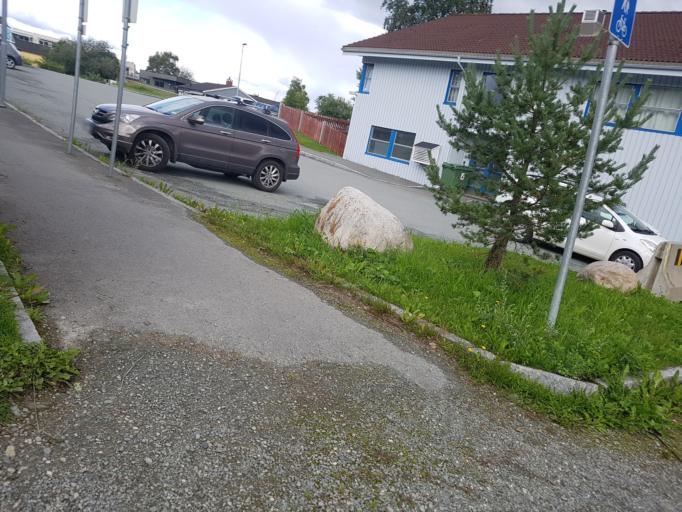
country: NO
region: Sor-Trondelag
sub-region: Trondheim
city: Trondheim
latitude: 63.4286
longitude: 10.4619
